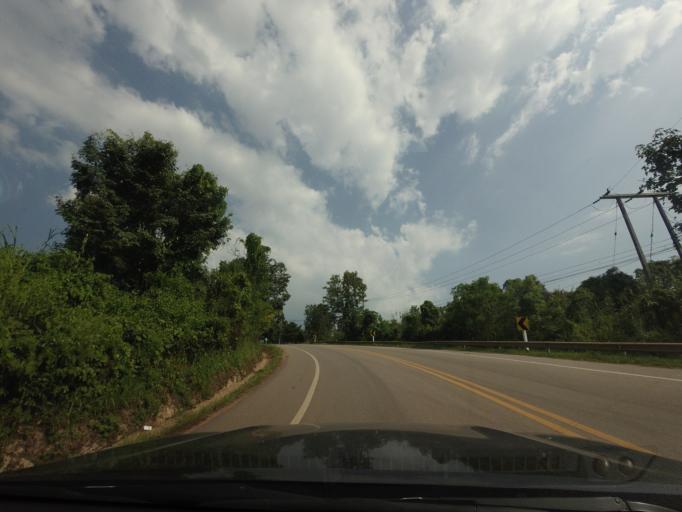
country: TH
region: Phitsanulok
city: Nakhon Thai
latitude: 17.0174
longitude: 100.9160
